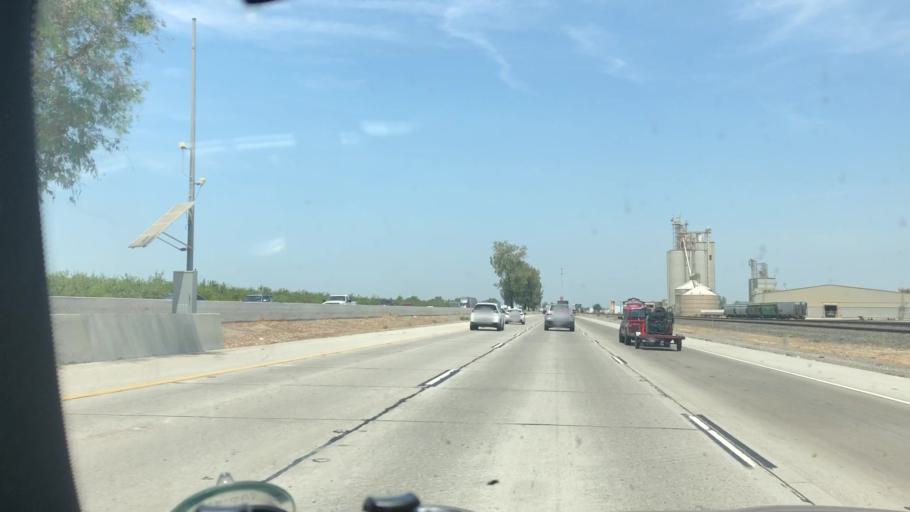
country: US
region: California
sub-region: Tulare County
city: London
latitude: 36.4384
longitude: -119.4787
